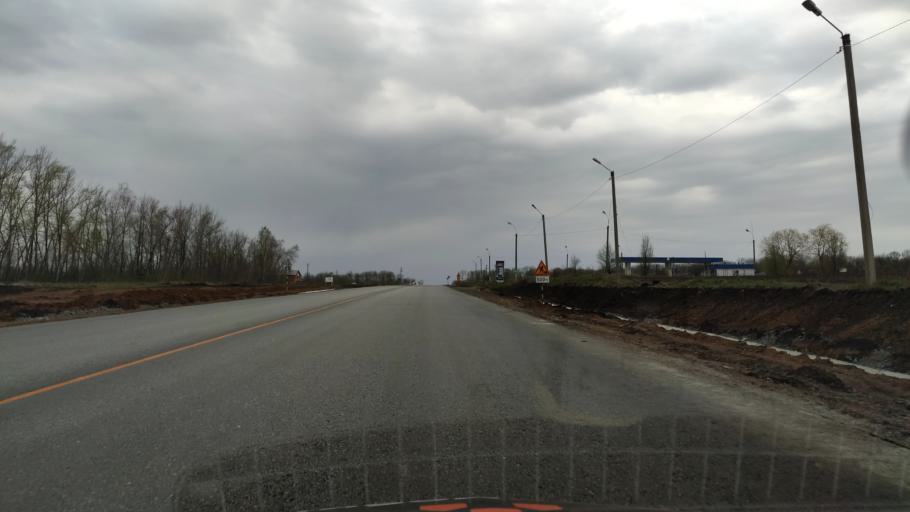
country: RU
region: Kursk
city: Gorshechnoye
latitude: 51.5495
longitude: 38.0487
